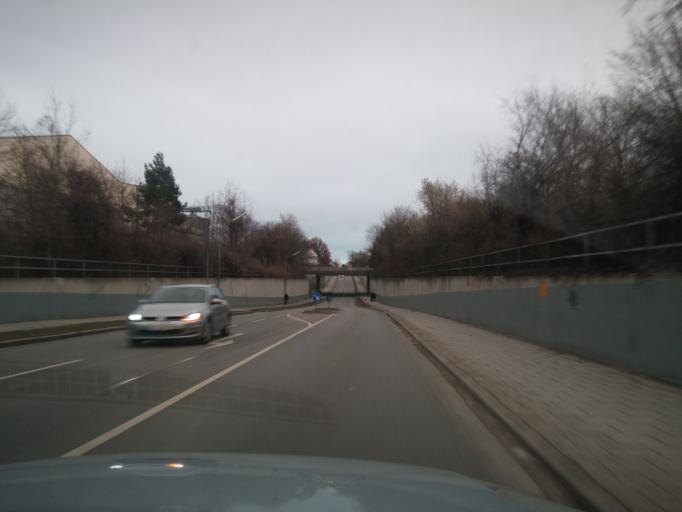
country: DE
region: Bavaria
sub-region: Upper Bavaria
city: Feldkirchen
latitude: 48.1518
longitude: 11.7262
